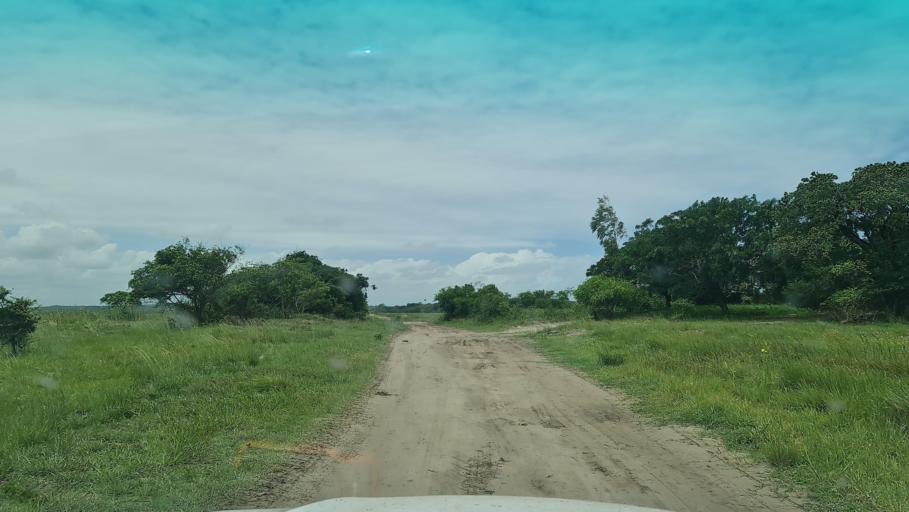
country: MZ
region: Maputo
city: Manhica
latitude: -25.5269
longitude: 32.8536
